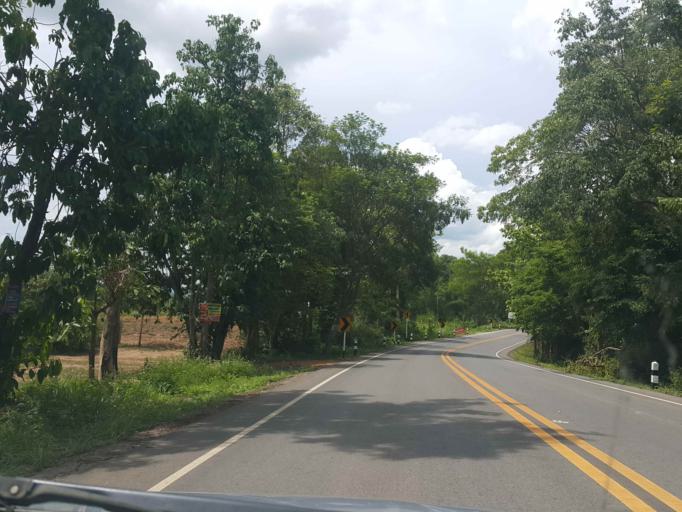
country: TH
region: Nan
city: Ban Luang
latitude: 18.8570
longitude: 100.4539
